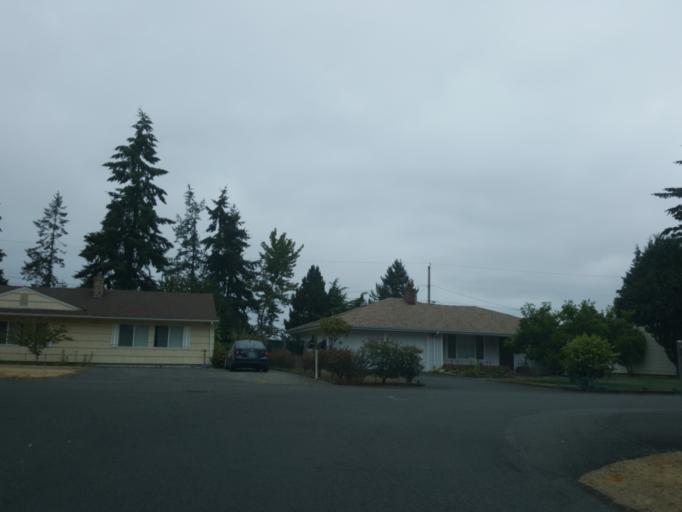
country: US
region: Washington
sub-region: Pierce County
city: Lakewood
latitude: 47.1659
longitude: -122.4902
